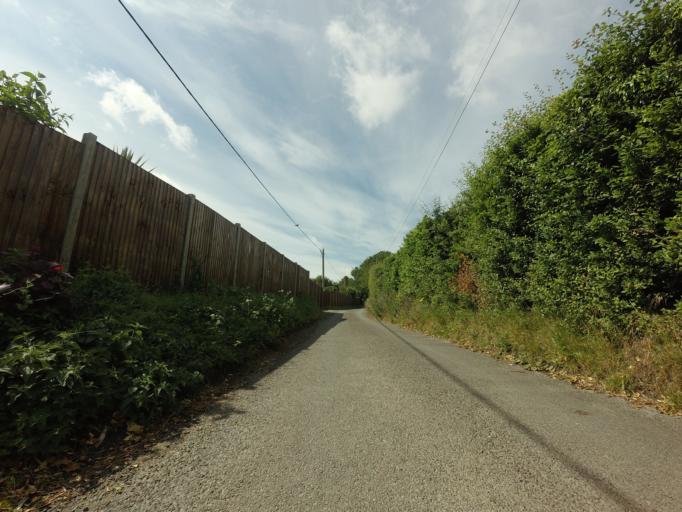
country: GB
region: England
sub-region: Greater London
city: Orpington
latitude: 51.3737
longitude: 0.1382
